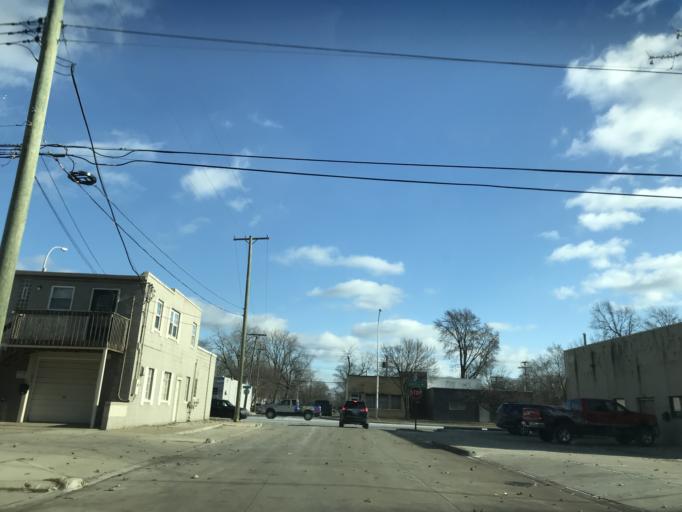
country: US
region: Michigan
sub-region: Oakland County
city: Madison Heights
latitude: 42.4791
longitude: -83.1056
